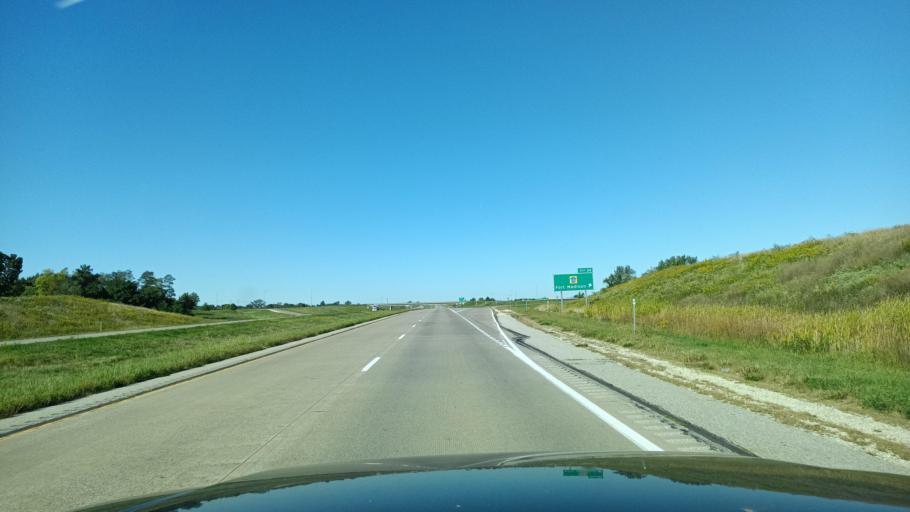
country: US
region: Iowa
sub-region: Lee County
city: Fort Madison
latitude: 40.6707
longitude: -91.3198
